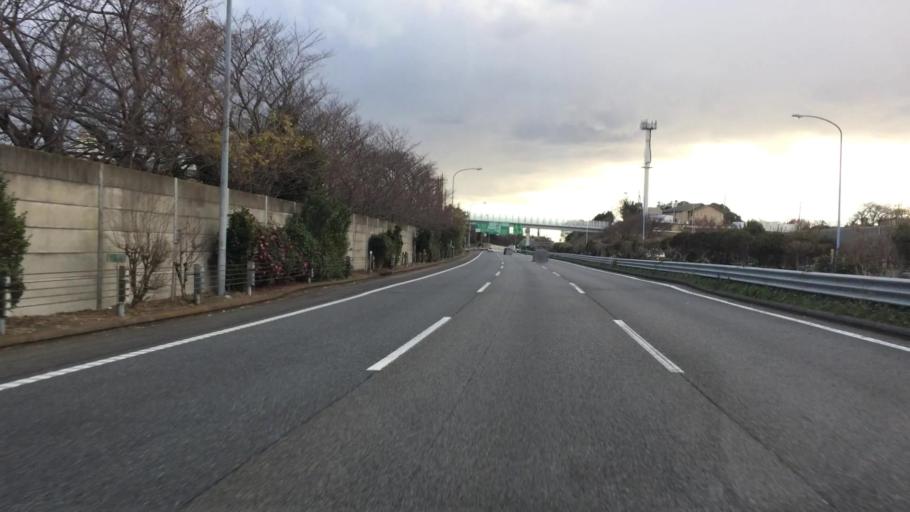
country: JP
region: Kanagawa
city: Yokohama
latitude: 35.4966
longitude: 139.5915
